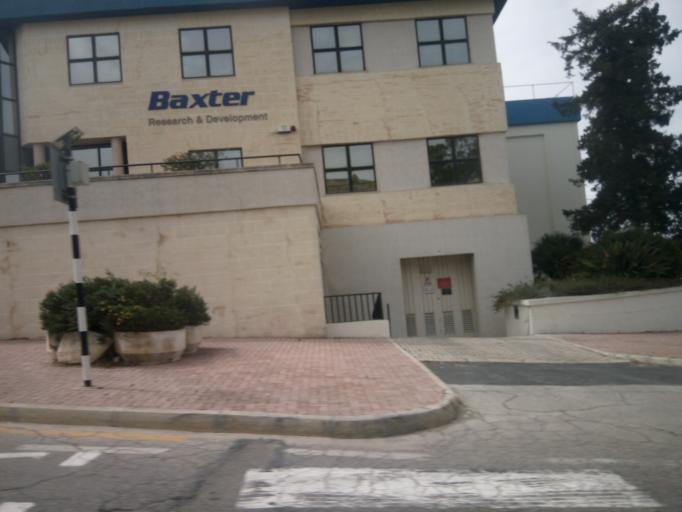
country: MT
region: Paola
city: Paola
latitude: 35.8691
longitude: 14.4897
